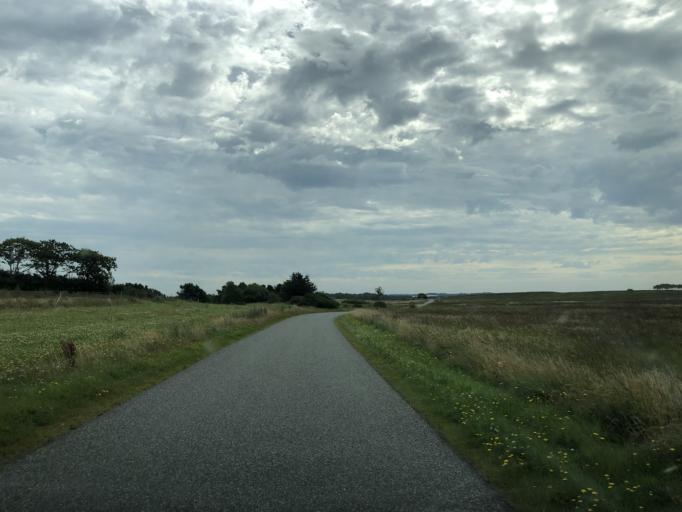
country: DK
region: Central Jutland
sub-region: Holstebro Kommune
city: Holstebro
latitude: 56.2714
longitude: 8.5120
